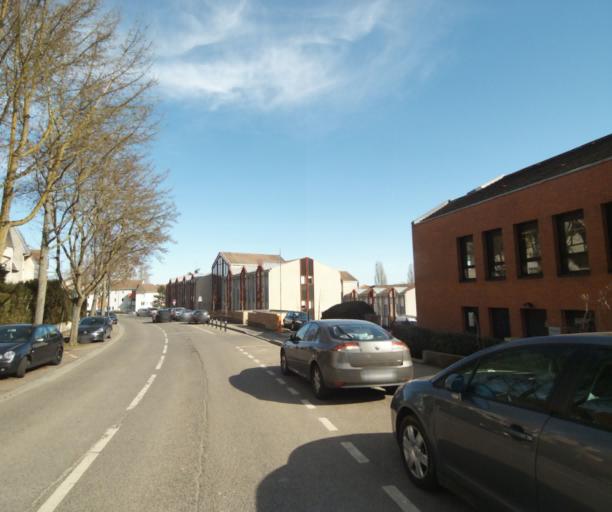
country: FR
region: Lorraine
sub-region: Departement de Meurthe-et-Moselle
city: Villers-les-Nancy
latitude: 48.6698
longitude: 6.1484
